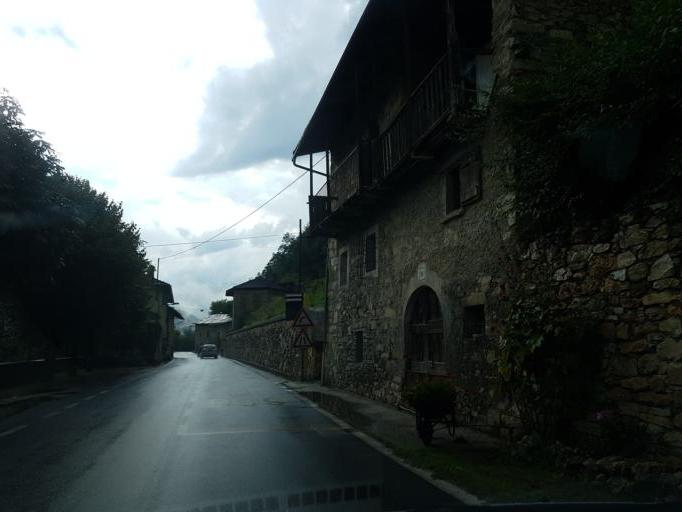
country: IT
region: Piedmont
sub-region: Provincia di Cuneo
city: Chiesa di Macra
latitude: 44.4920
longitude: 7.2175
